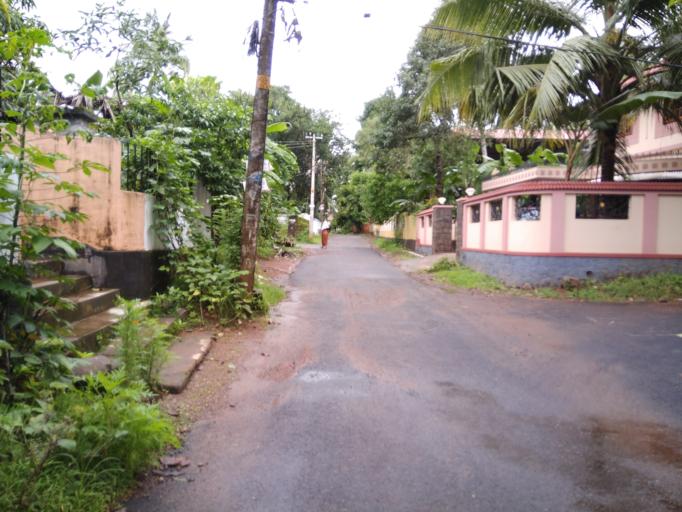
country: IN
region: Kerala
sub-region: Thrissur District
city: Avanoor
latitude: 10.5630
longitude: 76.1744
